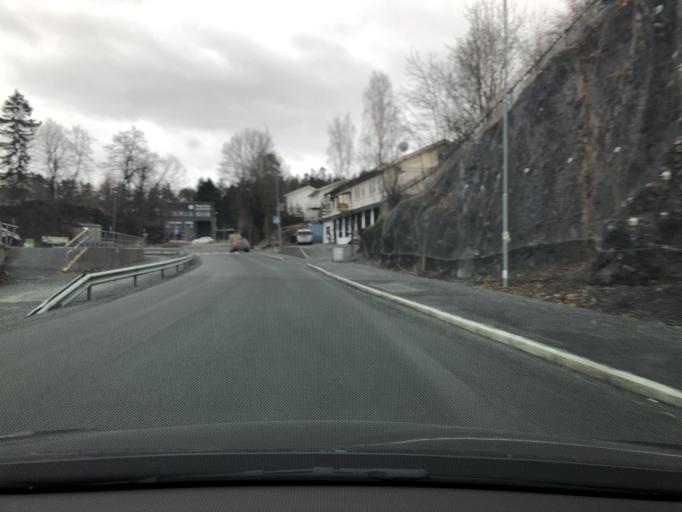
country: NO
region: Akershus
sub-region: Baerum
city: Sandvika
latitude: 59.8711
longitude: 10.5165
